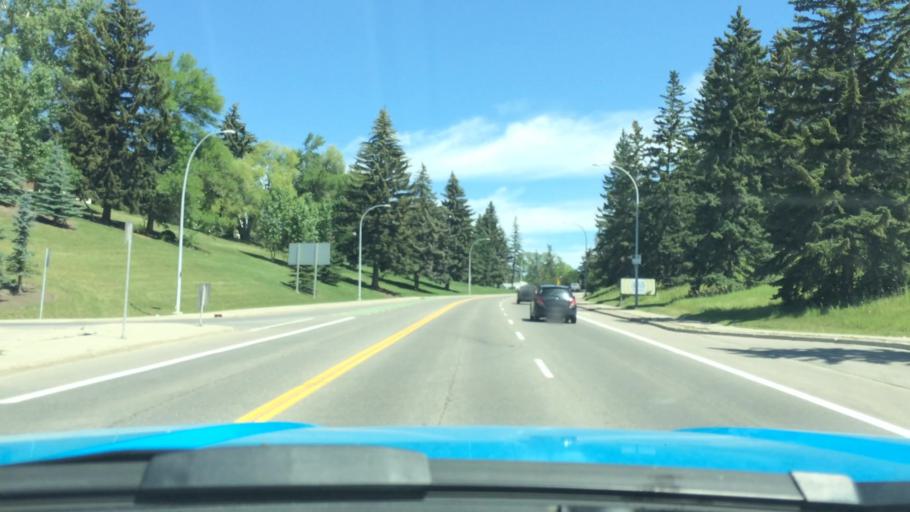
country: CA
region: Alberta
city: Calgary
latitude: 51.0615
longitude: -114.0858
